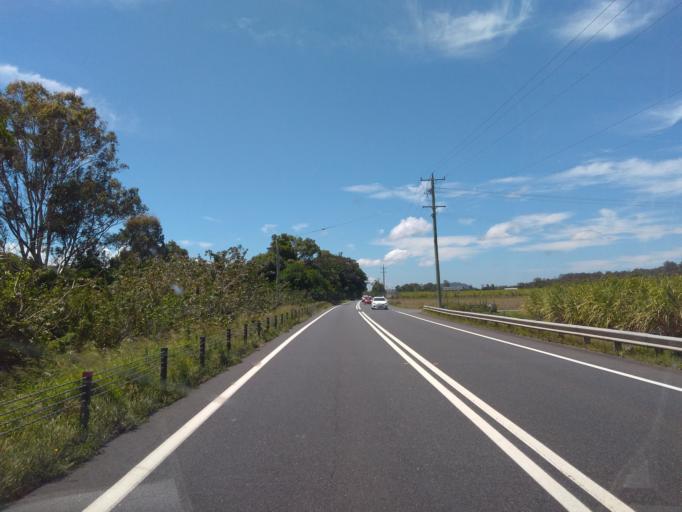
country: AU
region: New South Wales
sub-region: Clarence Valley
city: Maclean
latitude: -29.5192
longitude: 153.1863
